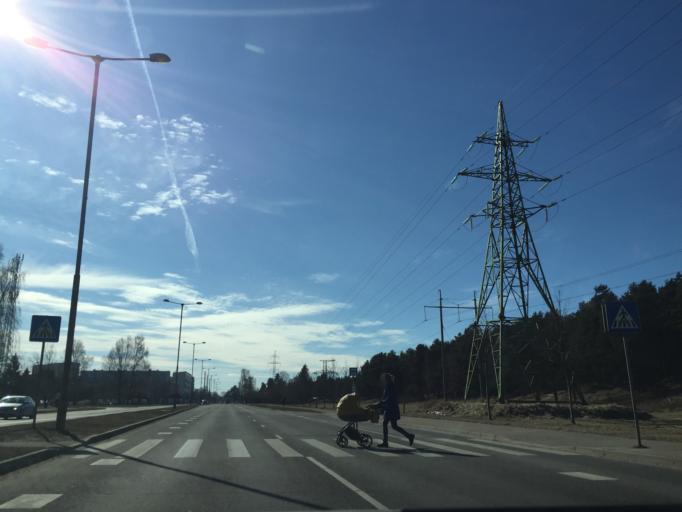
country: LV
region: Marupe
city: Marupe
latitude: 56.9683
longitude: 24.0103
